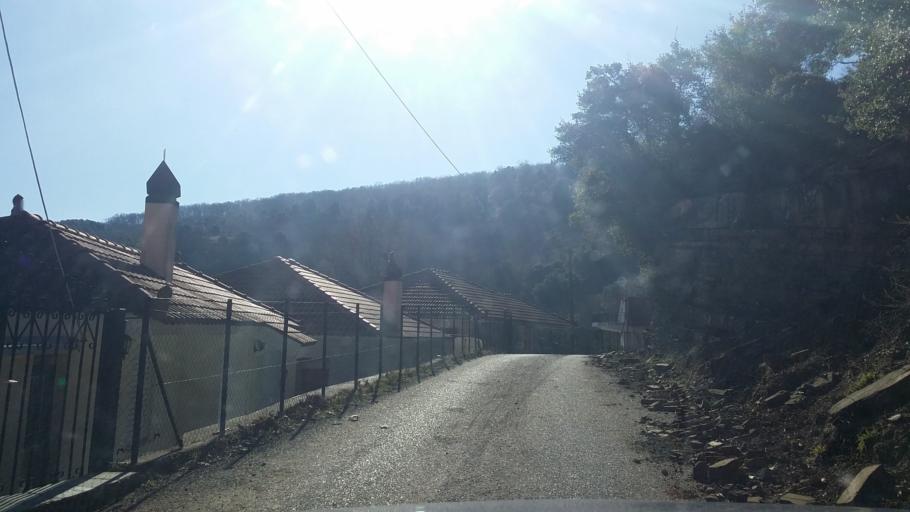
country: GR
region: West Greece
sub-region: Nomos Aitolias kai Akarnanias
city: Krikellos
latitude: 39.0113
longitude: 21.2686
